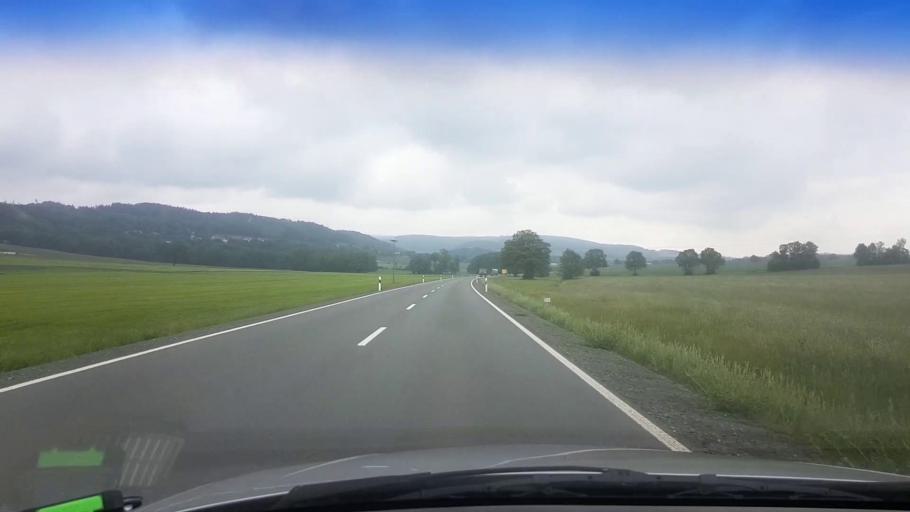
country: DE
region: Bavaria
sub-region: Upper Franconia
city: Gesees
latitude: 50.0280
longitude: 11.6564
